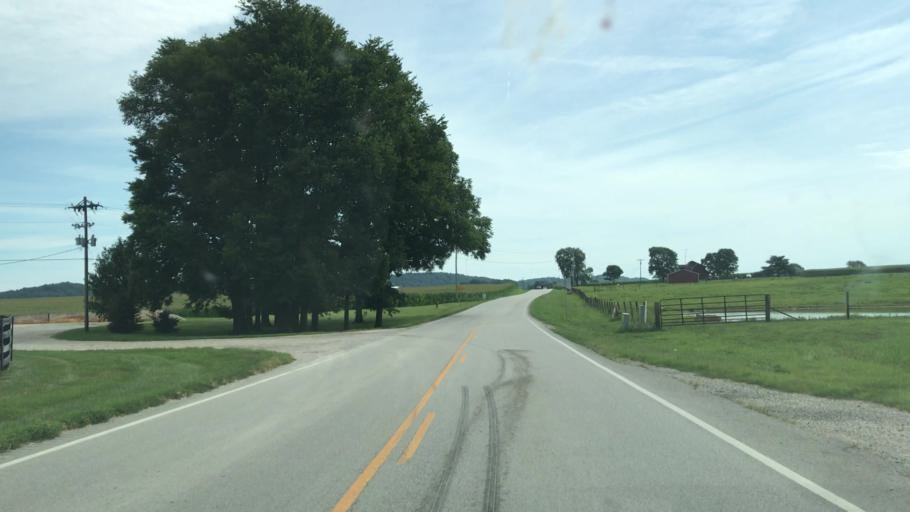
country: US
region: Kentucky
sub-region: Edmonson County
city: Brownsville
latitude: 37.0870
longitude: -86.2252
